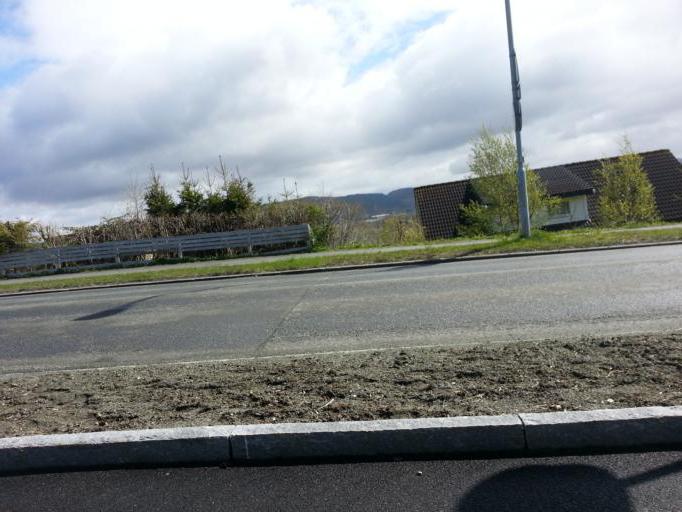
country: NO
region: Sor-Trondelag
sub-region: Trondheim
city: Trondheim
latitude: 63.3915
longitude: 10.3692
